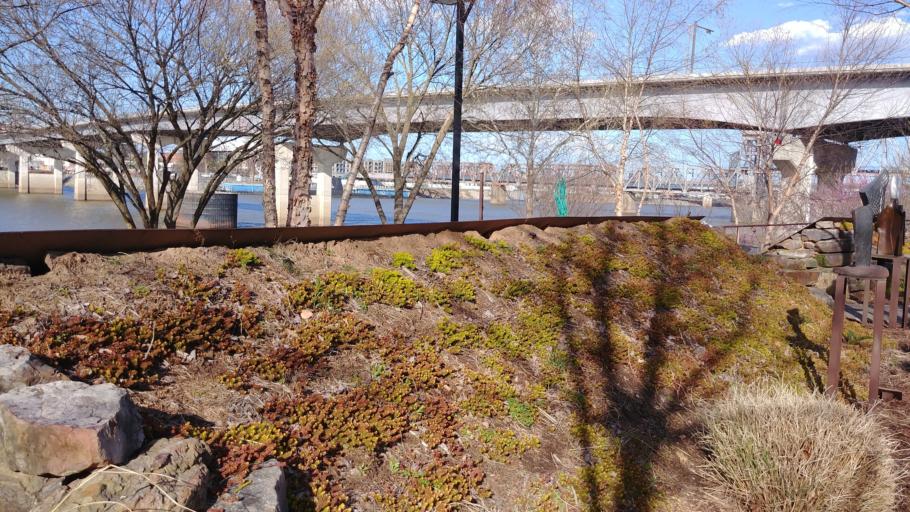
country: US
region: Arkansas
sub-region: Pulaski County
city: Little Rock
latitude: 34.7496
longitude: -92.2704
